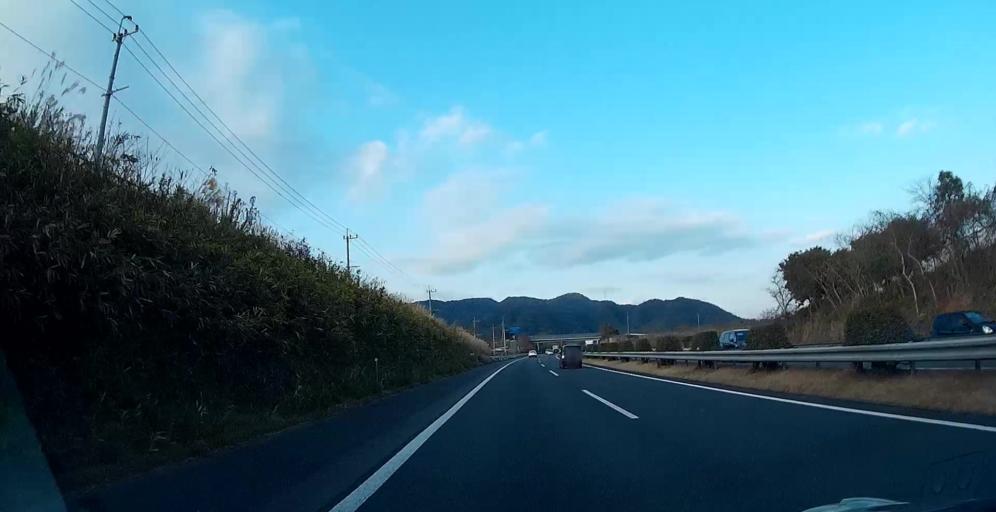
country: JP
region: Kumamoto
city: Matsubase
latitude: 32.6624
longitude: 130.7118
